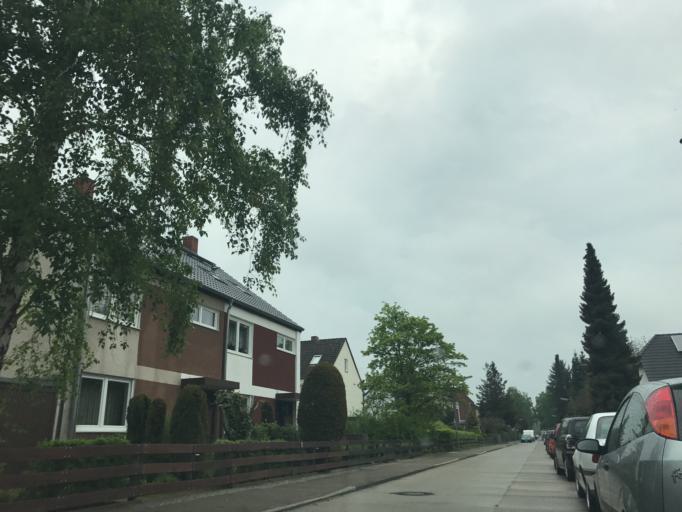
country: DE
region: Berlin
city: Staaken
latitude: 52.5482
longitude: 13.1506
